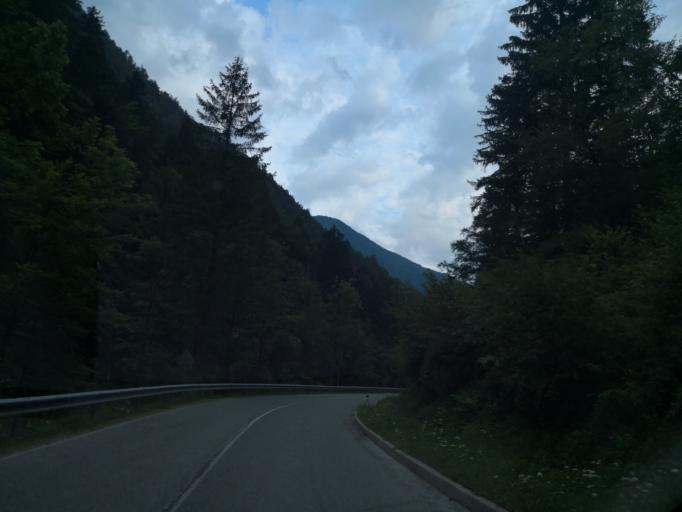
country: SI
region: Jezersko
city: Zgornje Jezersko
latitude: 46.3469
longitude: 14.4810
